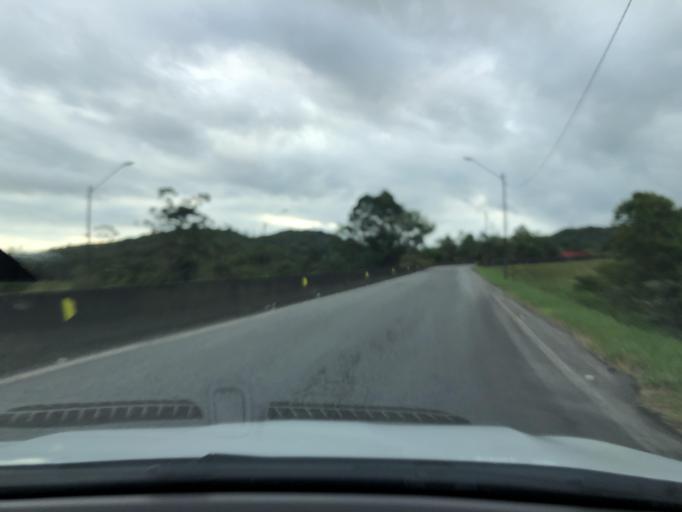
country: BR
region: Santa Catarina
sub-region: Joinville
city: Joinville
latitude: -26.4385
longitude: -48.8050
